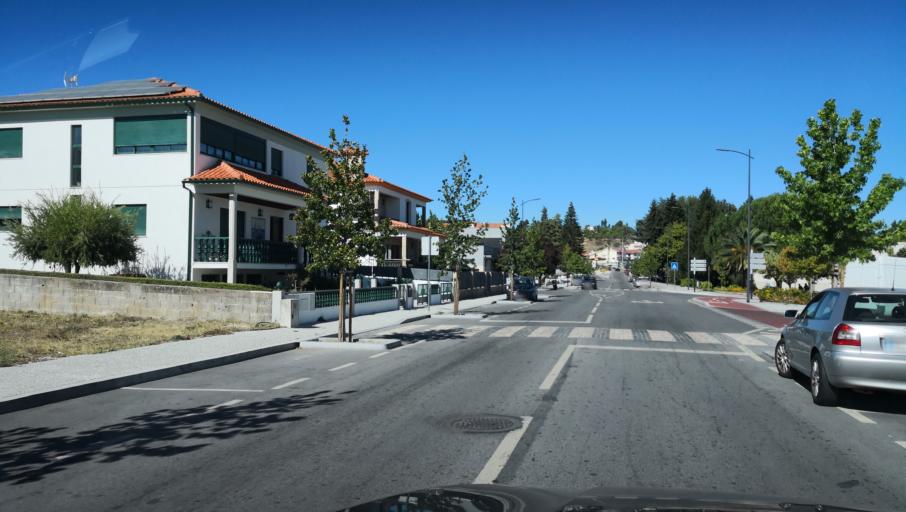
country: PT
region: Vila Real
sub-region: Valpacos
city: Valpacos
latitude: 41.6081
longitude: -7.3133
